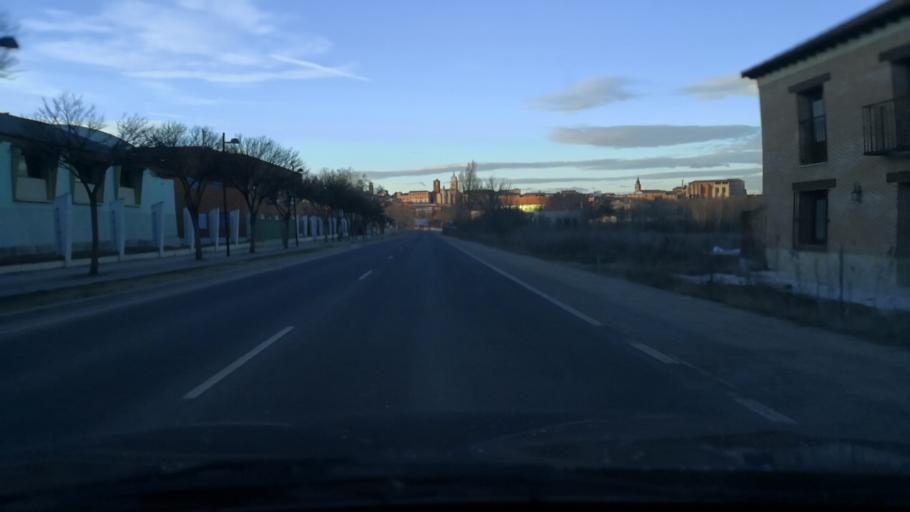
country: ES
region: Castille and Leon
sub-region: Provincia de Valladolid
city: Tordesillas
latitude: 41.4921
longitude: -4.9976
